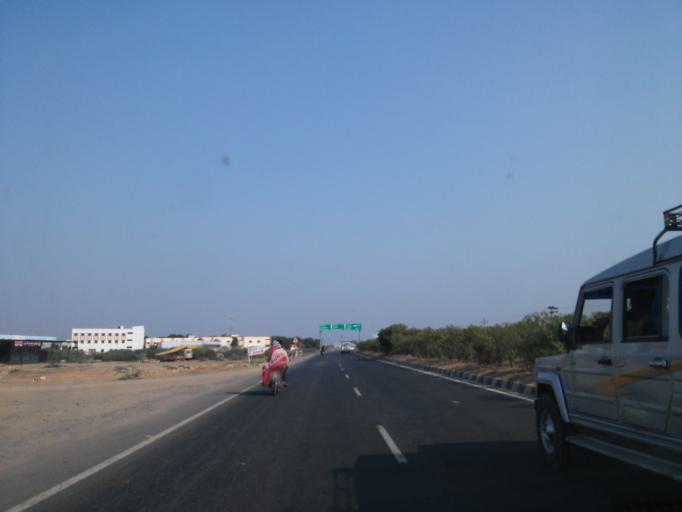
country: IN
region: Gujarat
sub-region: Surendranagar
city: Halvad
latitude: 23.0044
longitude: 71.1607
